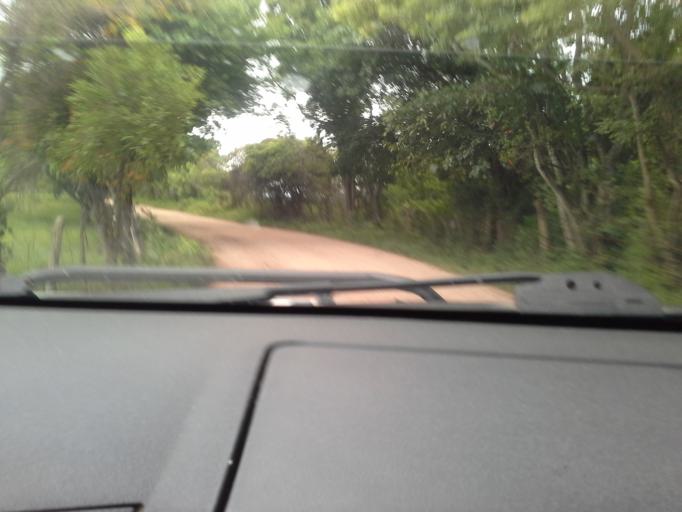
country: NI
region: Matagalpa
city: Ciudad Dario
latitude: 12.8340
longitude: -86.2096
